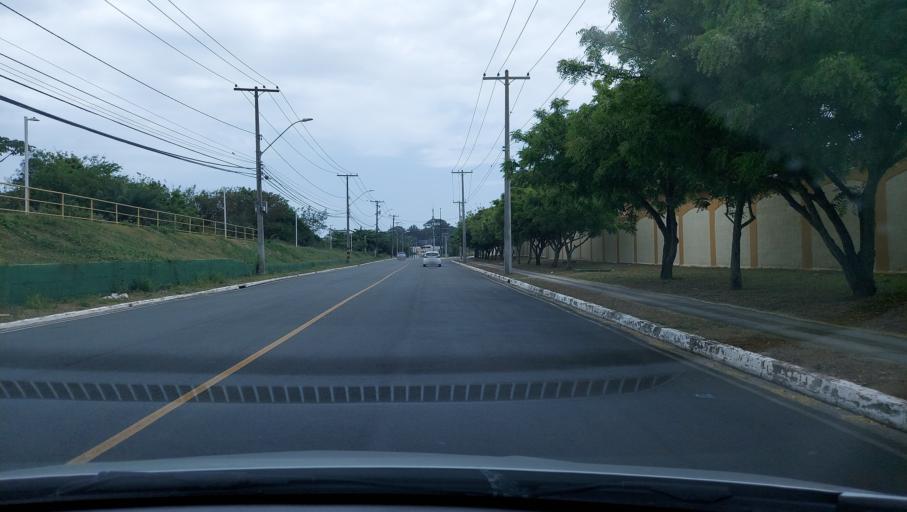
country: BR
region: Bahia
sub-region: Lauro De Freitas
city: Lauro de Freitas
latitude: -12.9509
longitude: -38.3907
